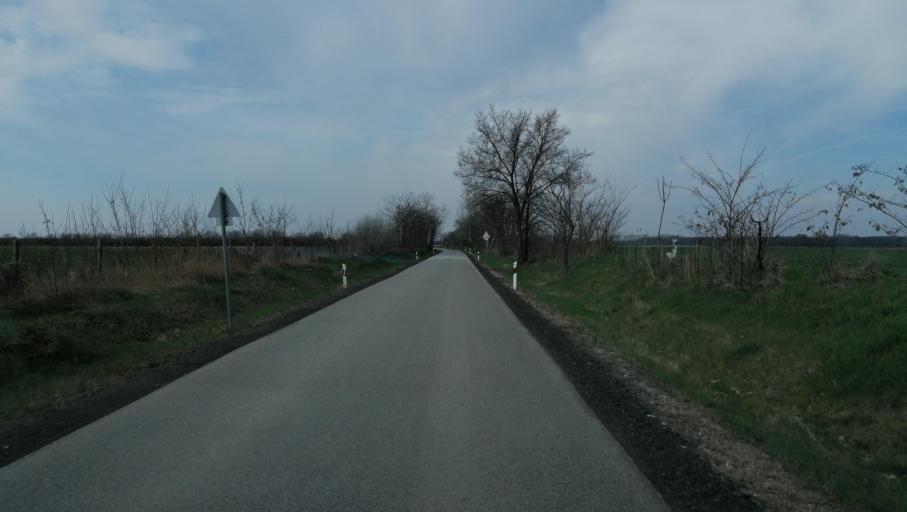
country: HU
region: Pest
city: Kiskunlachaza
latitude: 47.1913
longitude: 18.9882
